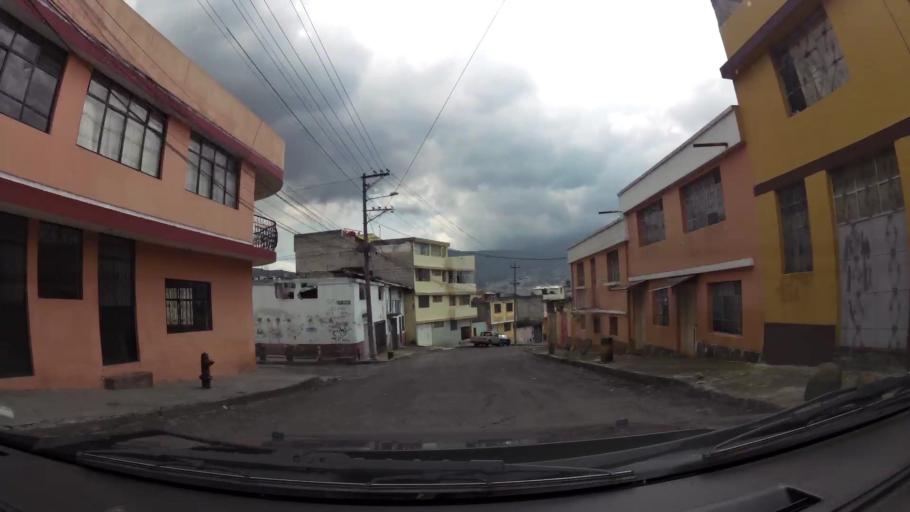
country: EC
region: Pichincha
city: Quito
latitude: -0.2534
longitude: -78.5132
